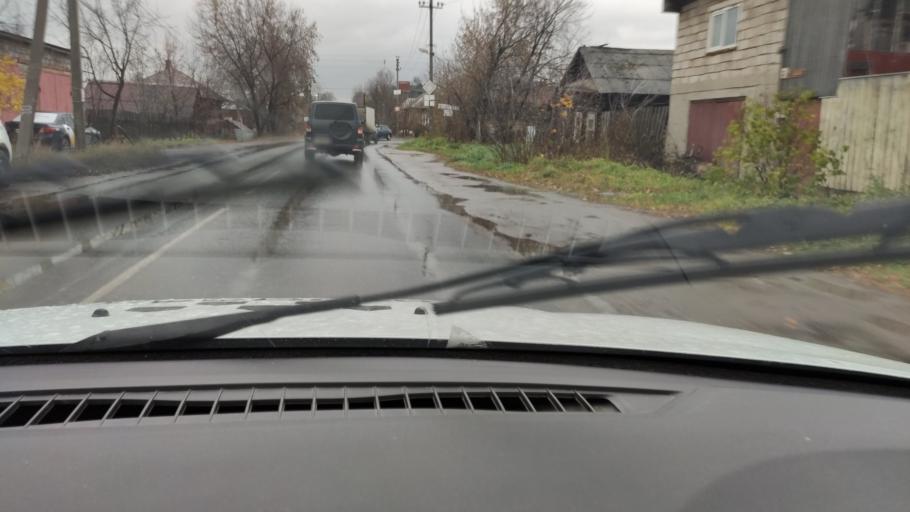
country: RU
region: Perm
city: Perm
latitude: 58.0359
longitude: 56.3428
